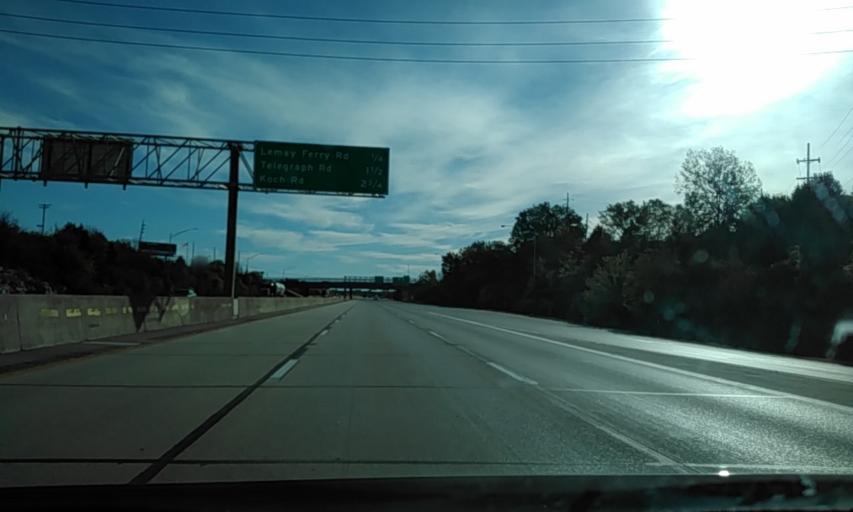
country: US
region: Missouri
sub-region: Saint Louis County
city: Mehlville
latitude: 38.5029
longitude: -90.3346
